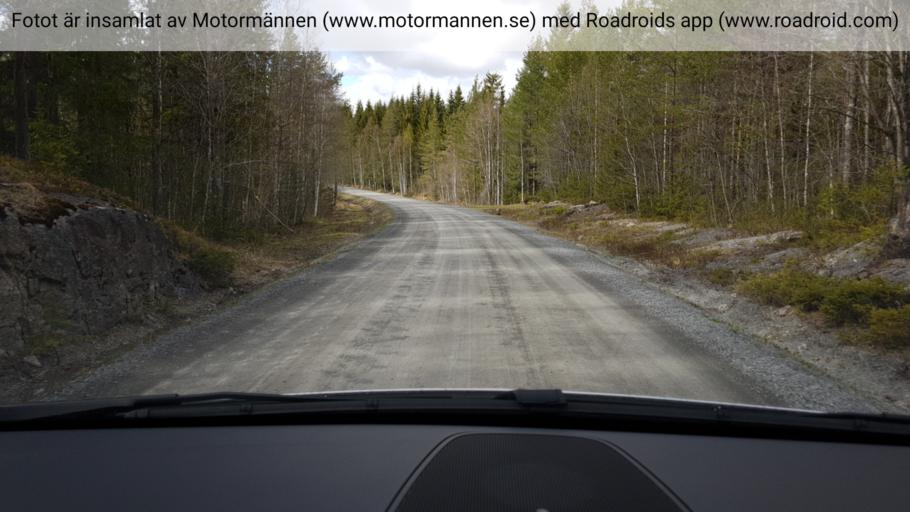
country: SE
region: Jaemtland
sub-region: OEstersunds Kommun
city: Brunflo
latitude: 63.1105
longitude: 15.0918
